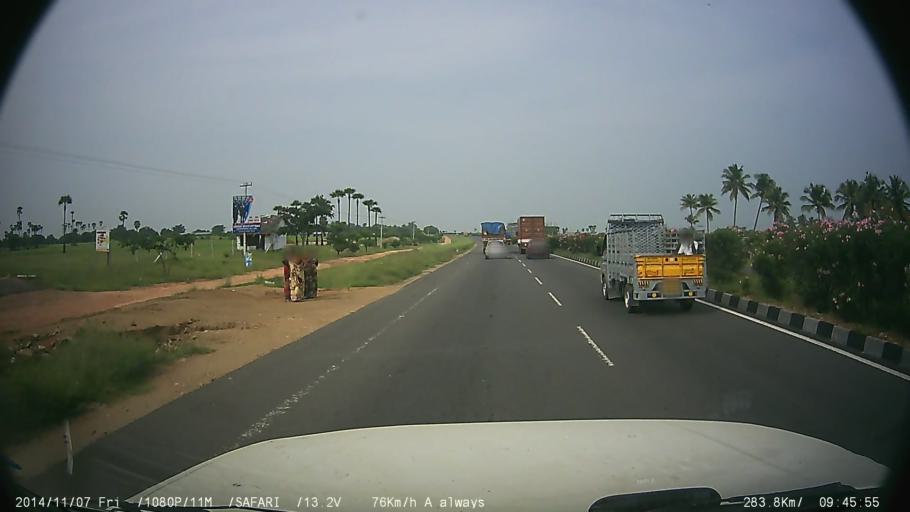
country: IN
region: Tamil Nadu
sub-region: Erode
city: Perundurai
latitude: 11.2915
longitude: 77.5757
